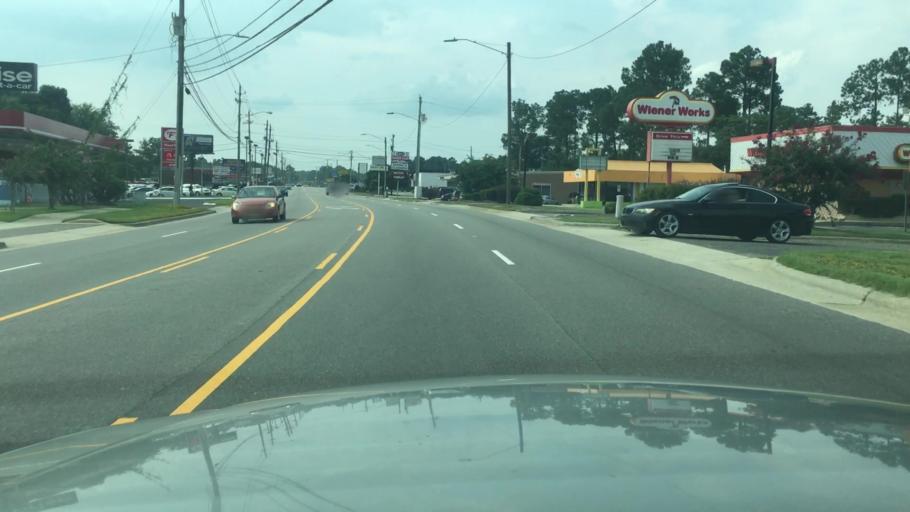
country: US
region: North Carolina
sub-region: Cumberland County
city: Fort Bragg
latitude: 35.1008
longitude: -78.9903
